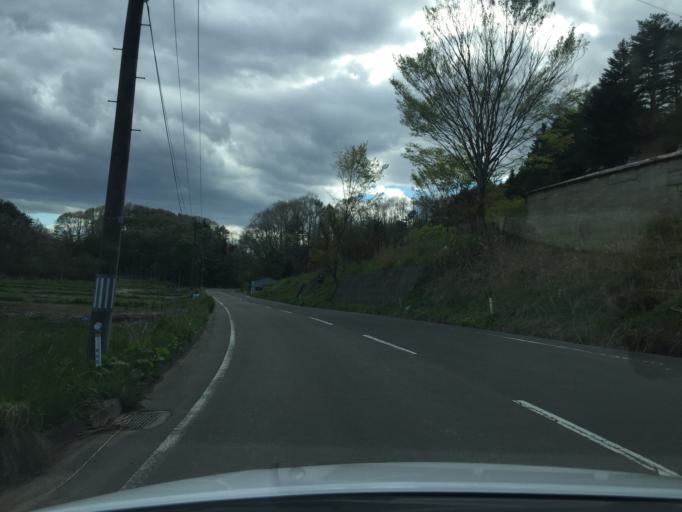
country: JP
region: Miyagi
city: Marumori
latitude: 37.7102
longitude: 140.7641
